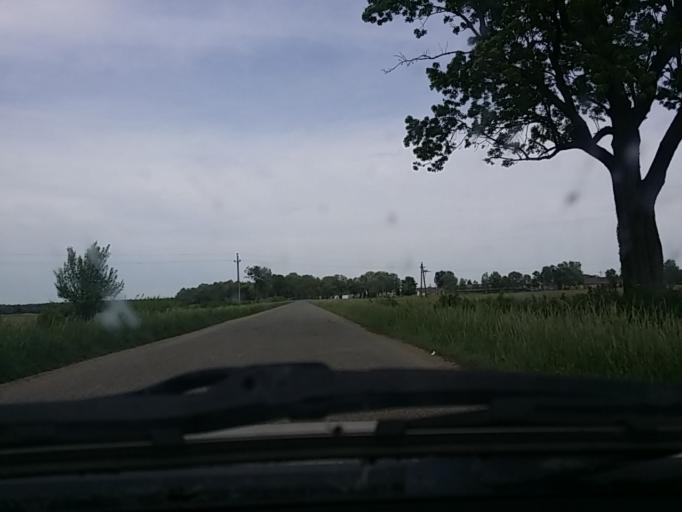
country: HU
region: Baranya
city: Sellye
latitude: 45.8561
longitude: 17.7097
